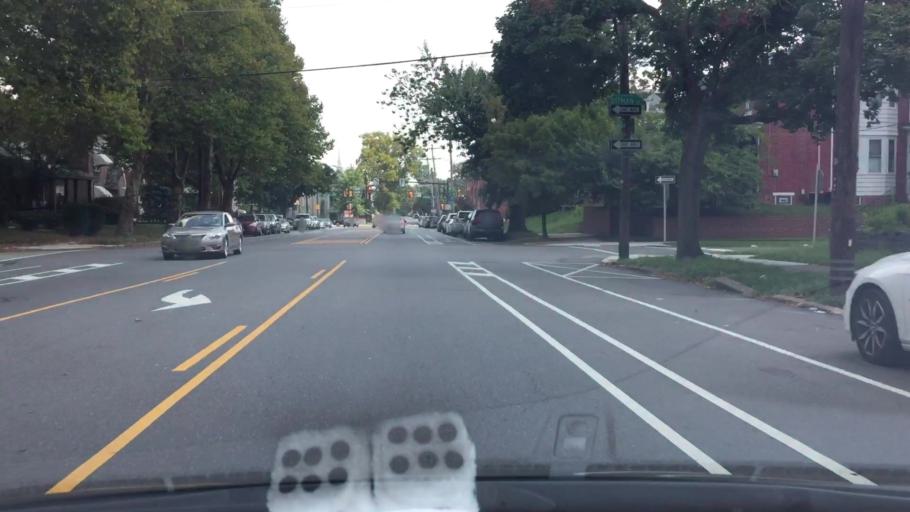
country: US
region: New Jersey
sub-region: Burlington County
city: Palmyra
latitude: 40.0284
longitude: -75.0422
